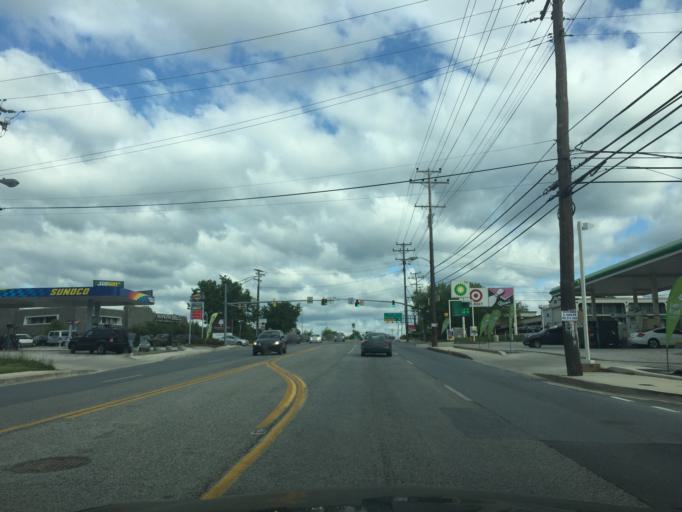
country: US
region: Maryland
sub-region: Baltimore County
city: Pikesville
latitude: 39.3821
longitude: -76.7310
